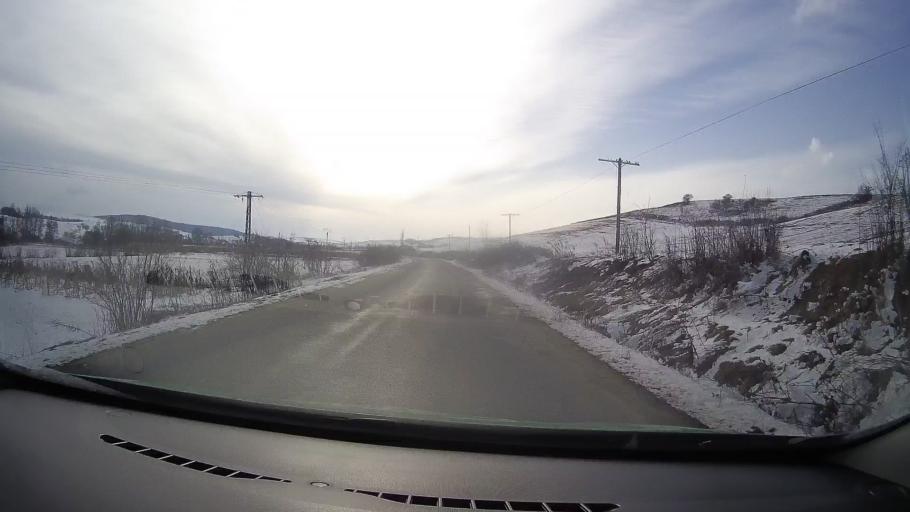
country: RO
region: Sibiu
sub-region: Oras Agnita
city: Ruja
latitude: 46.0145
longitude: 24.6901
